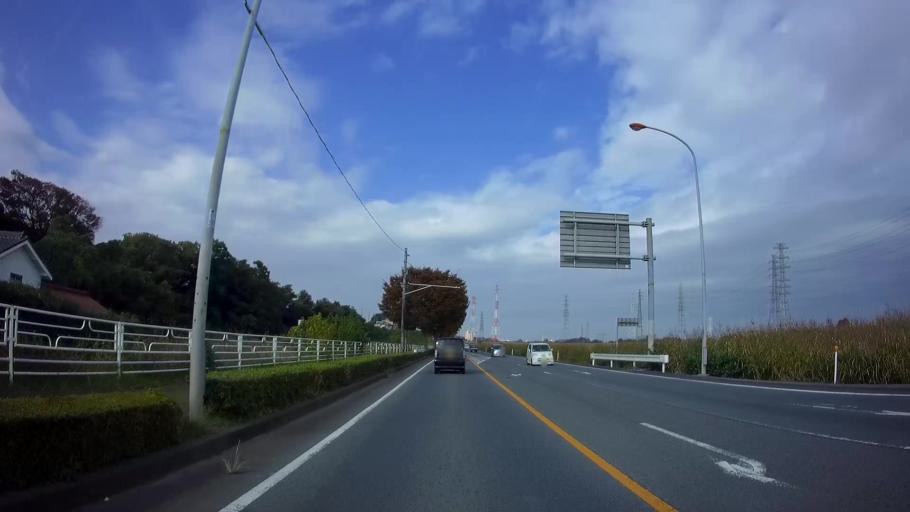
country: JP
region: Saitama
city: Honjo
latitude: 36.2211
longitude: 139.2347
